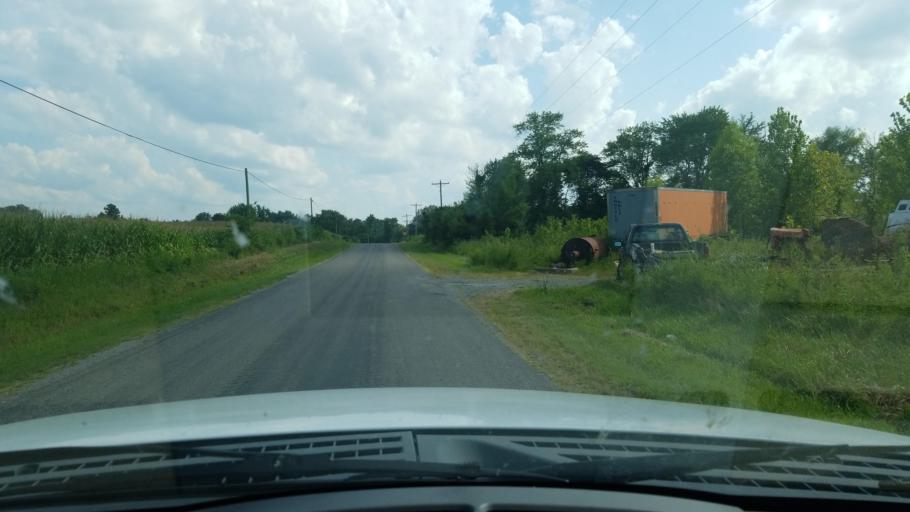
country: US
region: Illinois
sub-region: Saline County
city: Eldorado
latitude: 37.8335
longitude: -88.4317
